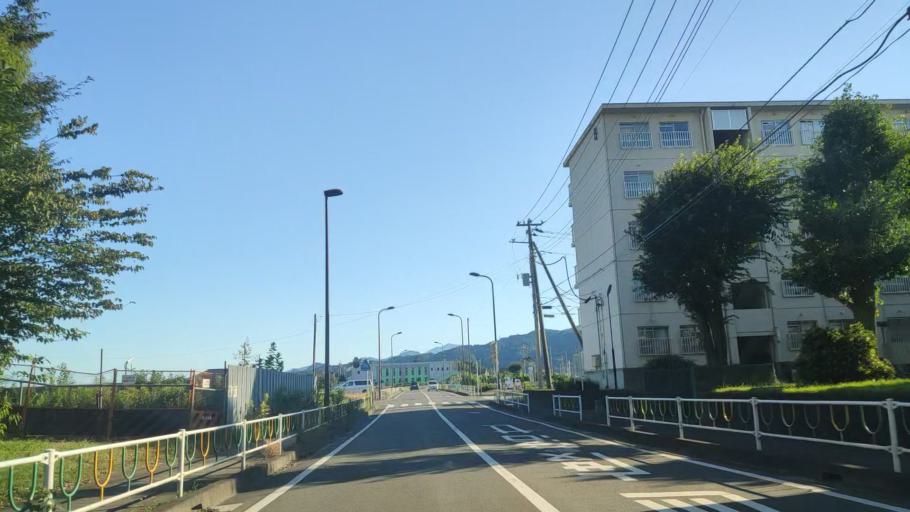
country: JP
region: Tokyo
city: Hachioji
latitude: 35.5851
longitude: 139.3140
